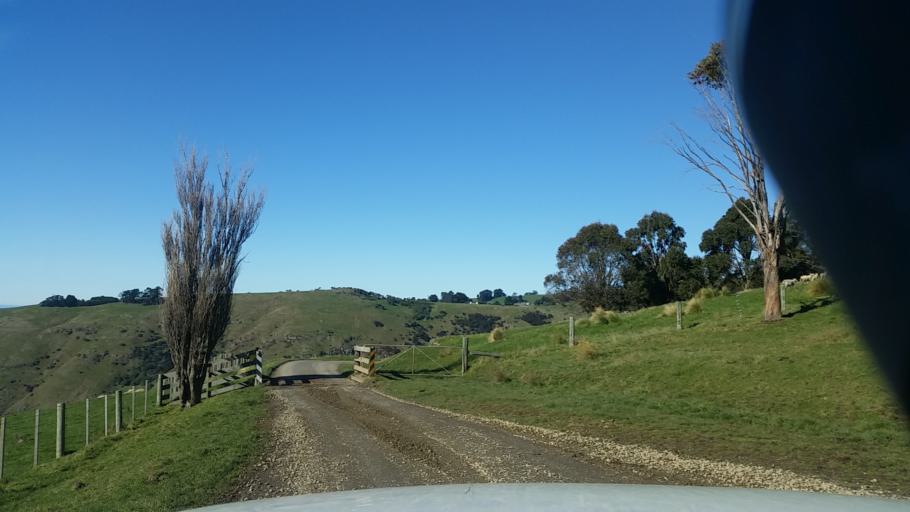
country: NZ
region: Canterbury
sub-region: Christchurch City
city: Christchurch
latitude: -43.6619
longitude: 172.9974
